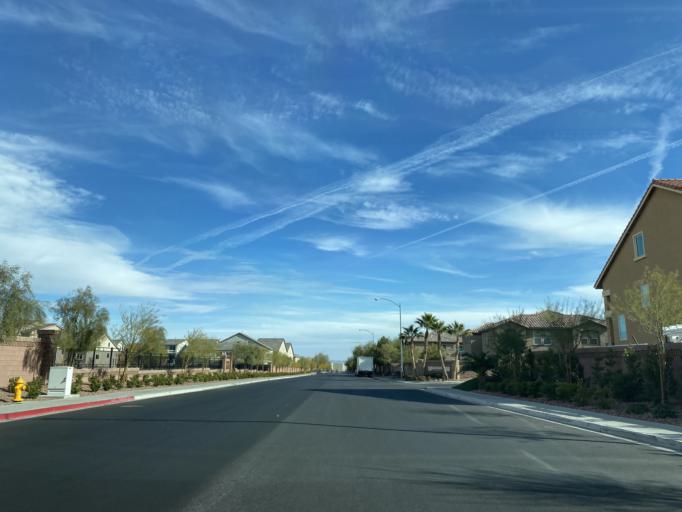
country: US
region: Nevada
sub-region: Clark County
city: Enterprise
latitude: 36.0598
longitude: -115.2322
